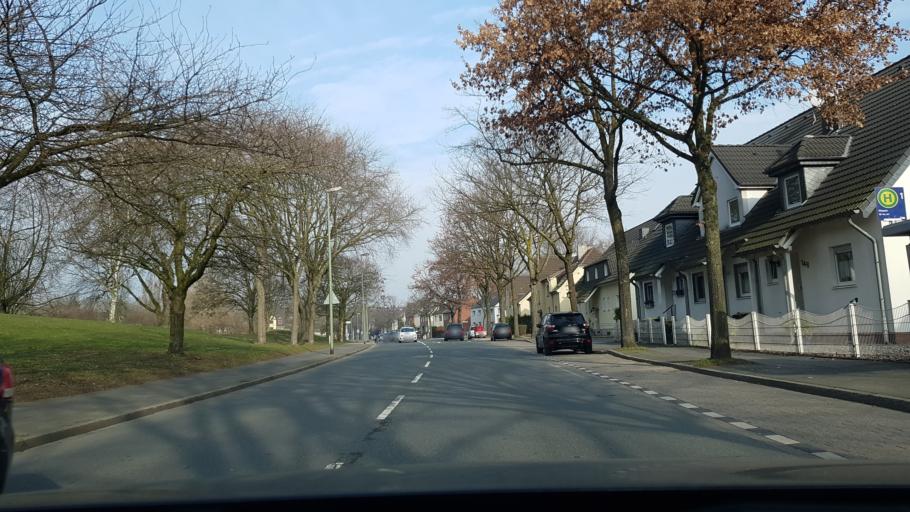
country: DE
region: North Rhine-Westphalia
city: Meiderich
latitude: 51.5006
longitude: 6.7974
